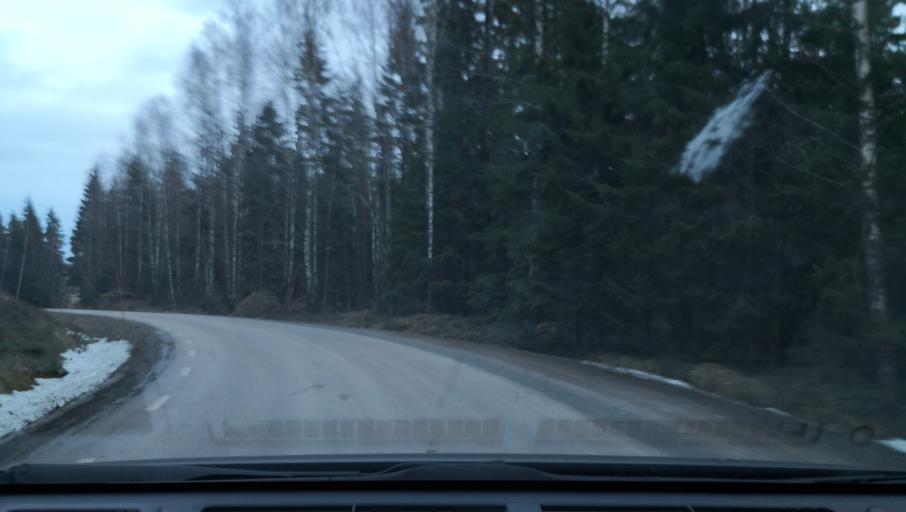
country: SE
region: OErebro
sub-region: Lindesbergs Kommun
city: Fellingsbro
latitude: 59.5490
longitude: 15.6267
